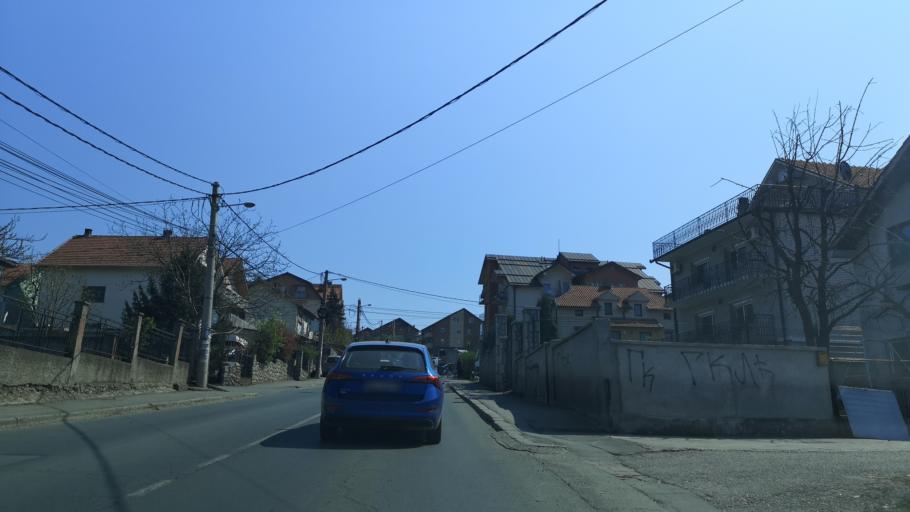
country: RS
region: Central Serbia
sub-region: Belgrade
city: Zvezdara
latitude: 44.7639
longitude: 20.5513
